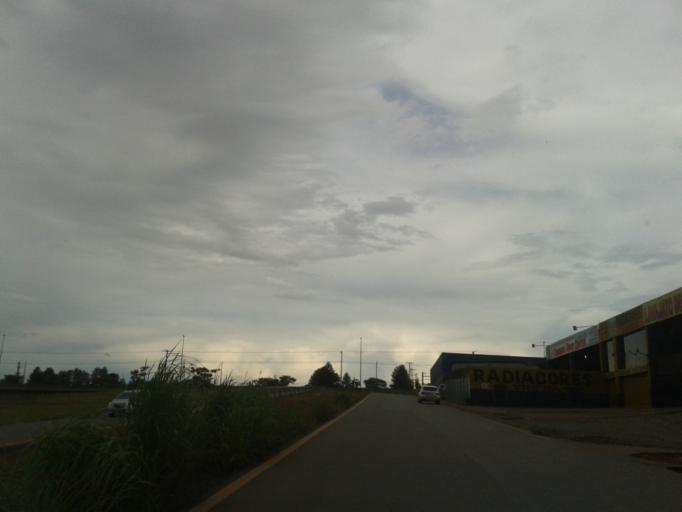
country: BR
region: Goias
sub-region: Aparecida De Goiania
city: Aparecida de Goiania
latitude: -16.7879
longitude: -49.2396
